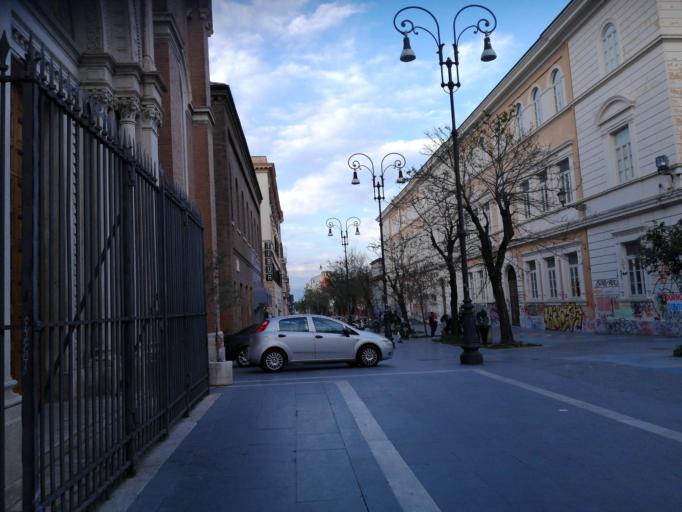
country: IT
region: Latium
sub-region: Citta metropolitana di Roma Capitale
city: Rome
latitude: 41.8967
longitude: 12.5148
